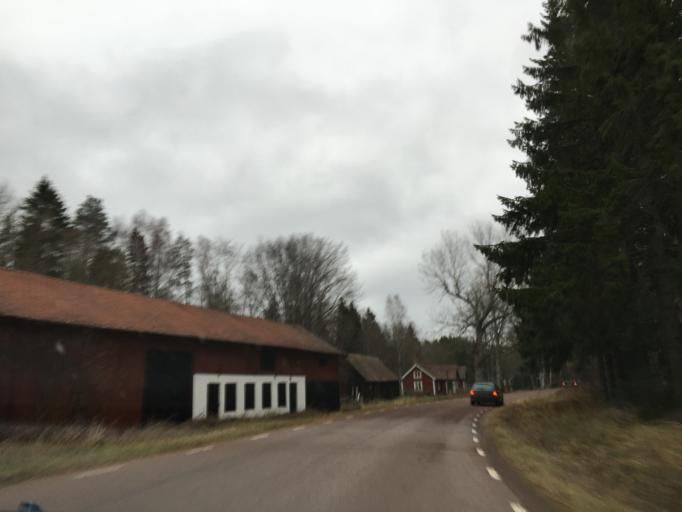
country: SE
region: Uppsala
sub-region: Alvkarleby Kommun
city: AElvkarleby
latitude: 60.6471
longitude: 17.5264
